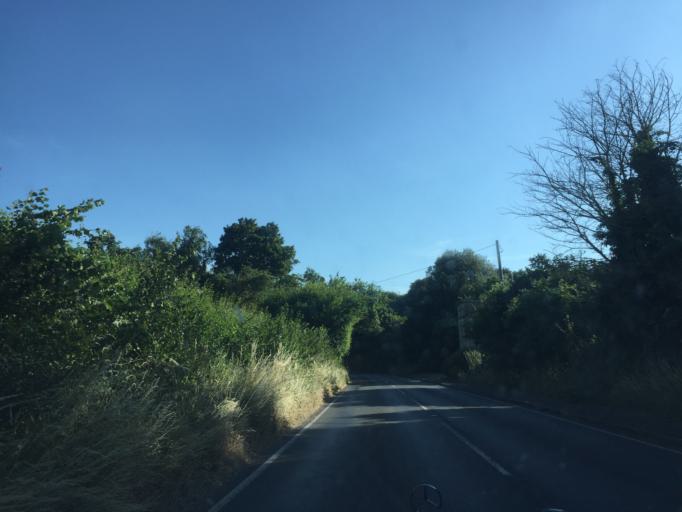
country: GB
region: England
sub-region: Oxfordshire
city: Watlington
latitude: 51.6551
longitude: -0.9937
